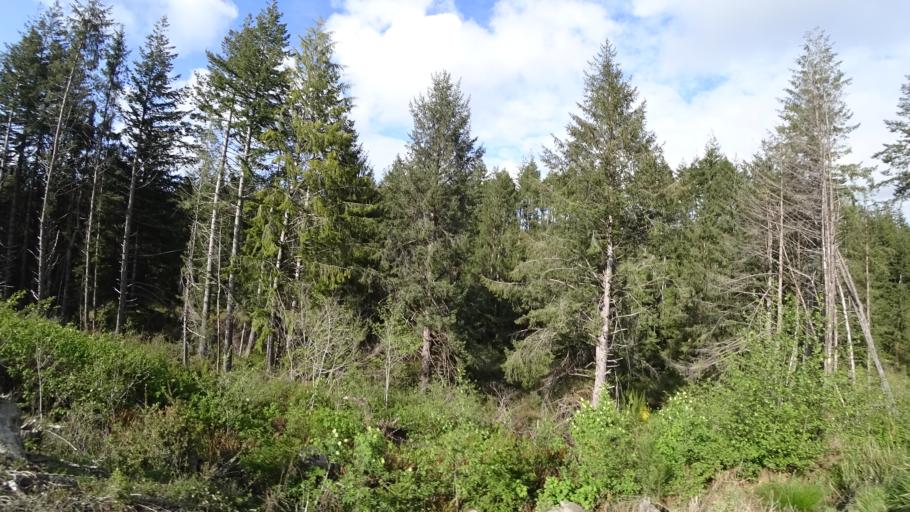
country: US
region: Oregon
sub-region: Douglas County
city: Reedsport
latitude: 43.7577
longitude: -124.1311
